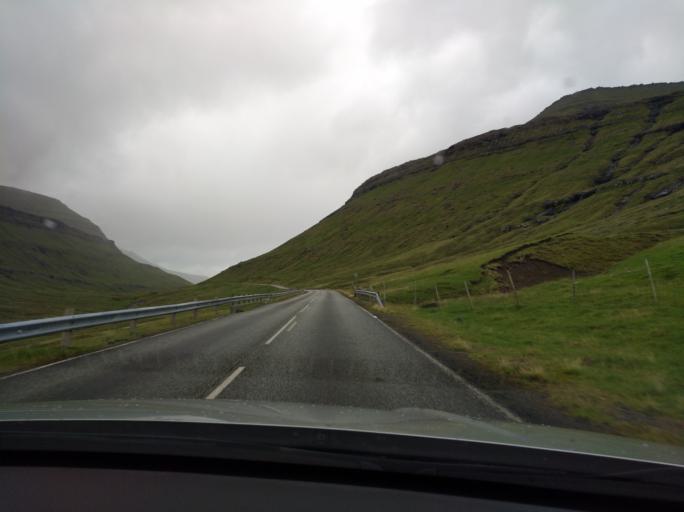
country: FO
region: Eysturoy
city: Fuglafjordur
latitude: 62.2251
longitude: -6.8799
